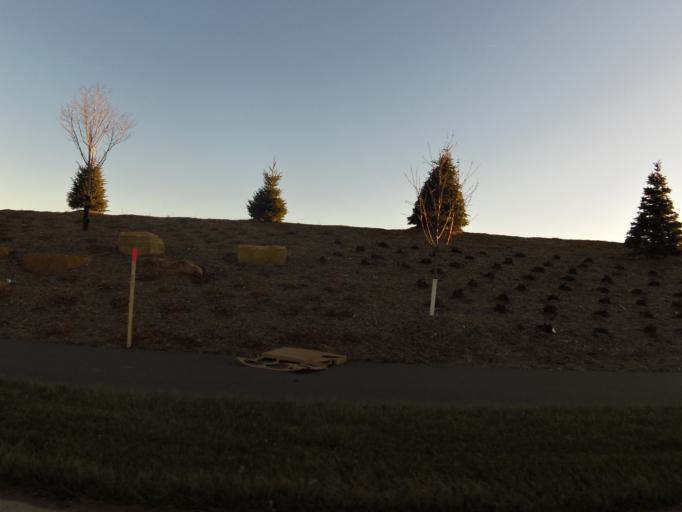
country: US
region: Wisconsin
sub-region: Saint Croix County
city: Hudson
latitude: 44.9682
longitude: -92.7240
